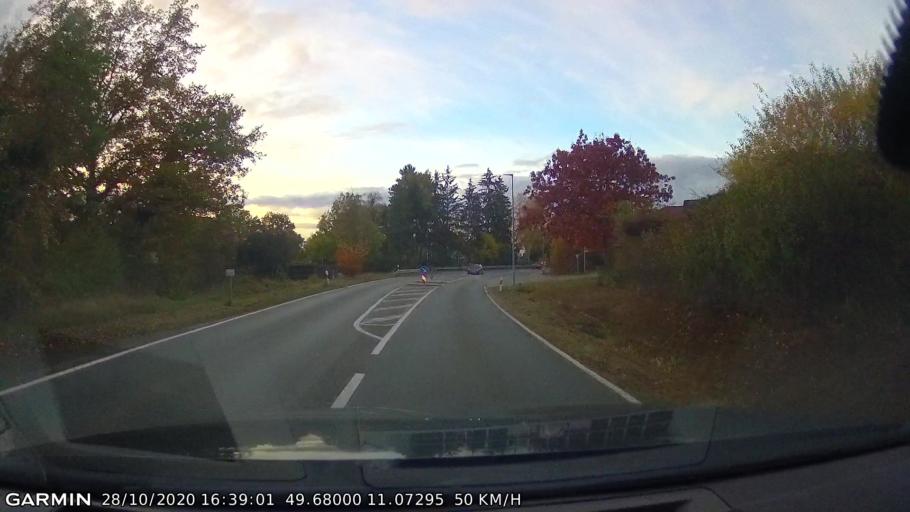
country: DE
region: Bavaria
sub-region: Upper Franconia
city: Poxdorf
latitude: 49.6801
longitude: 11.0729
